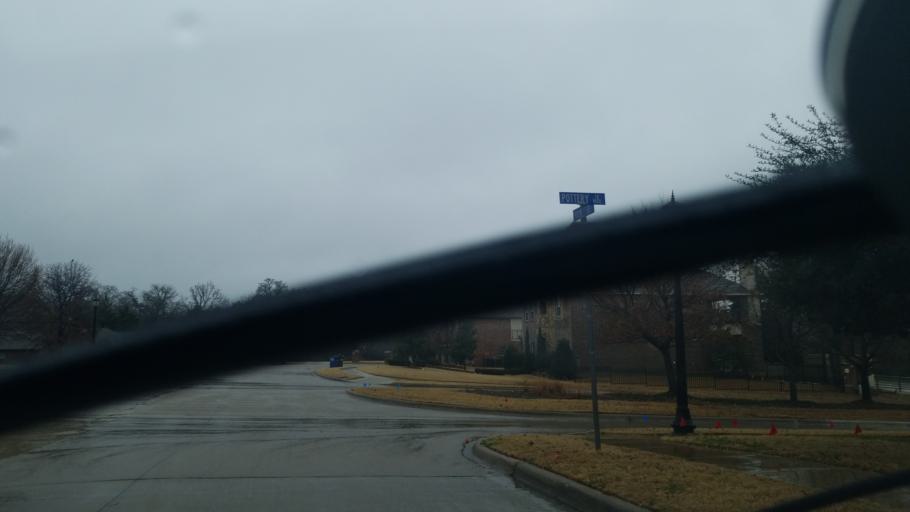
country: US
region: Texas
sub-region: Denton County
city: Corinth
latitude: 33.1348
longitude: -97.0936
